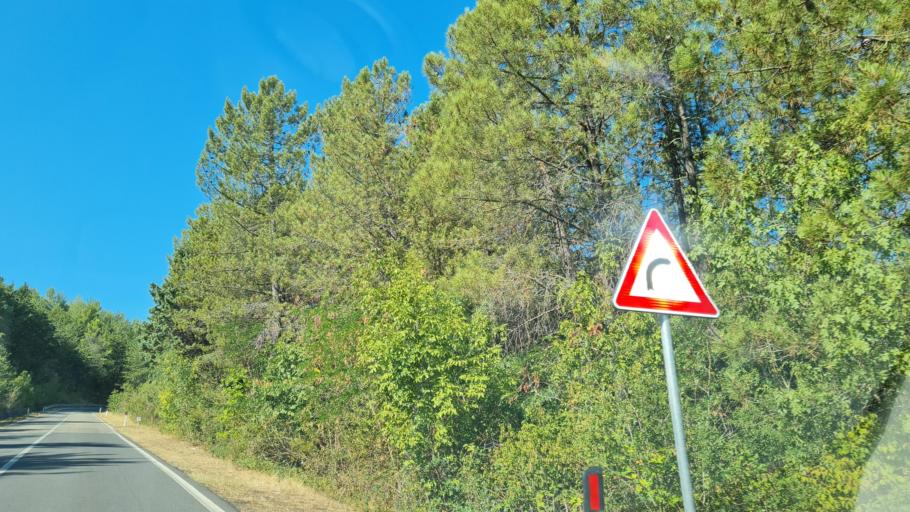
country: IT
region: Tuscany
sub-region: Provincia di Siena
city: Abbadia San Salvatore
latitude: 42.9257
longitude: 11.6988
